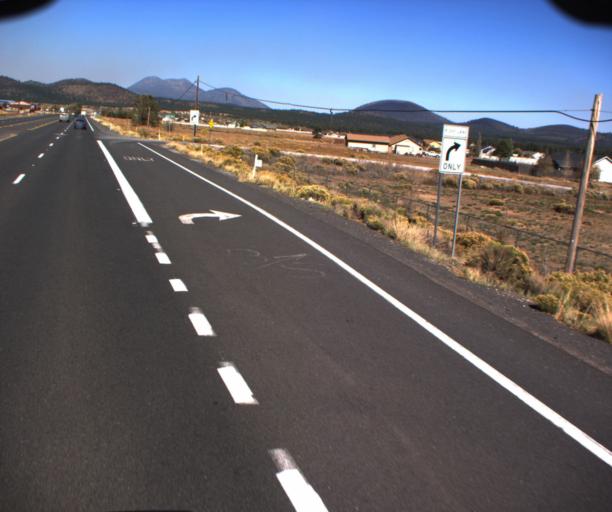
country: US
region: Arizona
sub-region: Coconino County
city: Flagstaff
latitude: 35.2979
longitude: -111.5426
